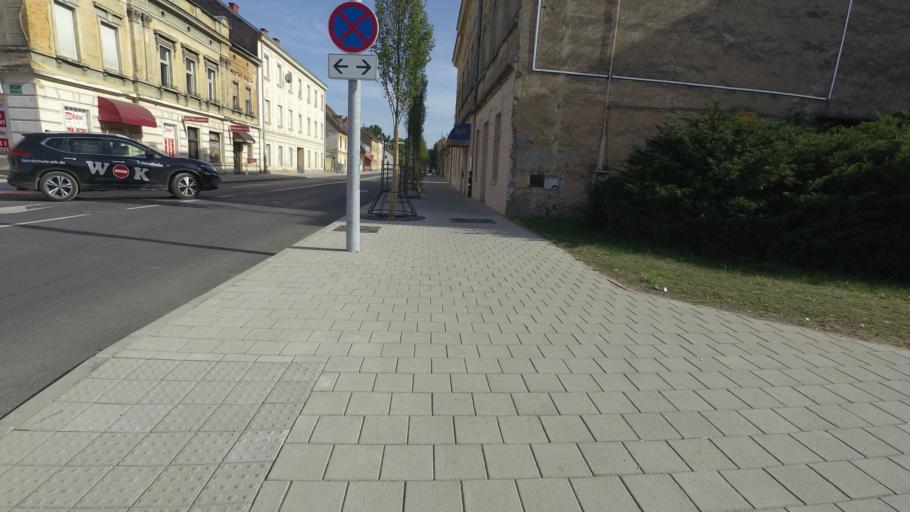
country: HR
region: Karlovacka
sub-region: Grad Karlovac
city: Karlovac
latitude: 45.4849
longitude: 15.5566
